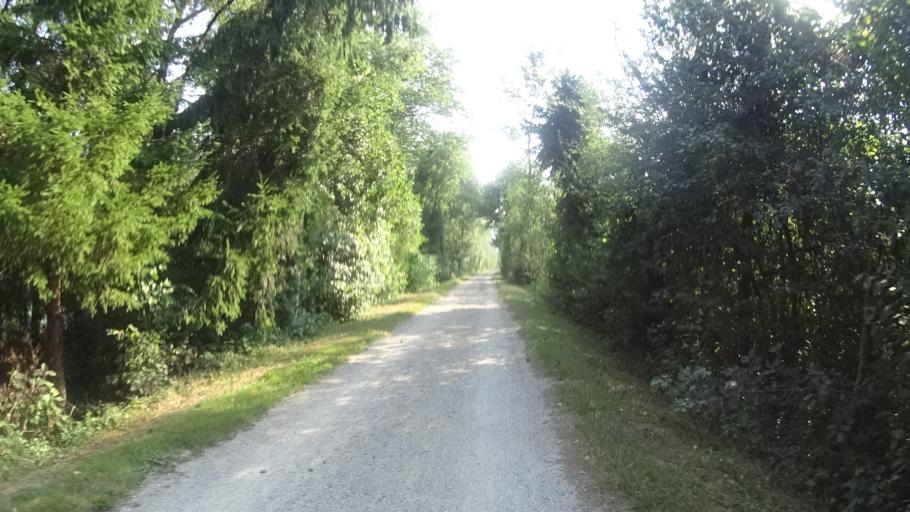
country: AT
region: Carinthia
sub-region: Politischer Bezirk Klagenfurt Land
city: Kottmannsdorf
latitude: 46.5413
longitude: 14.2002
